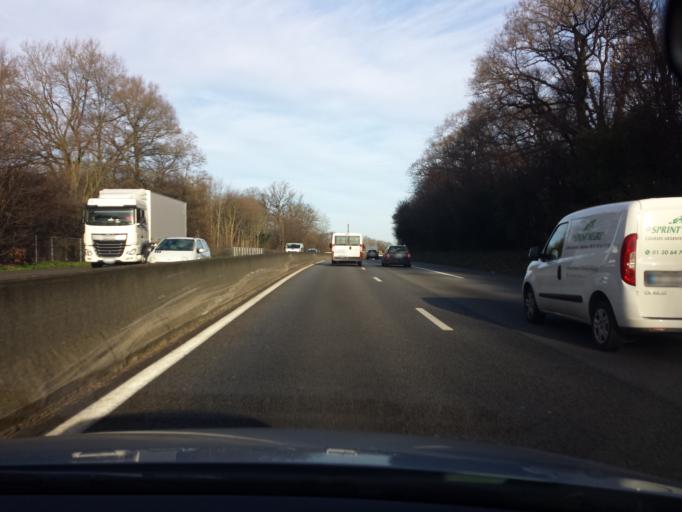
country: FR
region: Ile-de-France
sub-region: Departement des Yvelines
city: Orgeval
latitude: 48.8989
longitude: 2.0056
